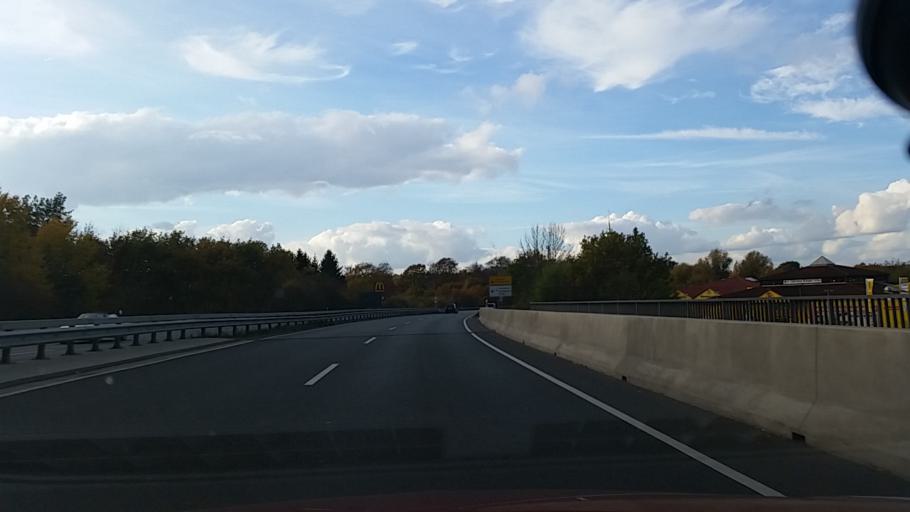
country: DE
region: Lower Saxony
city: Uelzen
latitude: 52.9866
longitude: 10.5516
